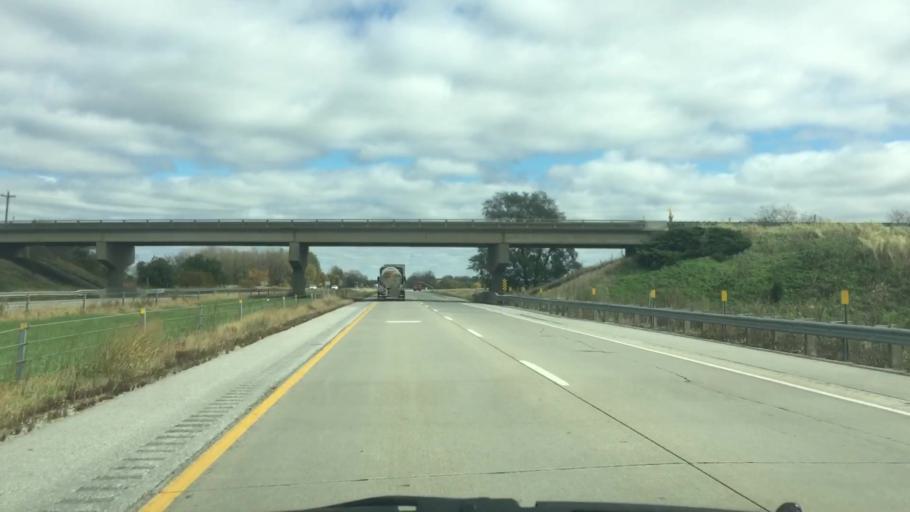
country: US
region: Iowa
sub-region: Jasper County
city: Colfax
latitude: 41.6919
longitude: -93.2476
